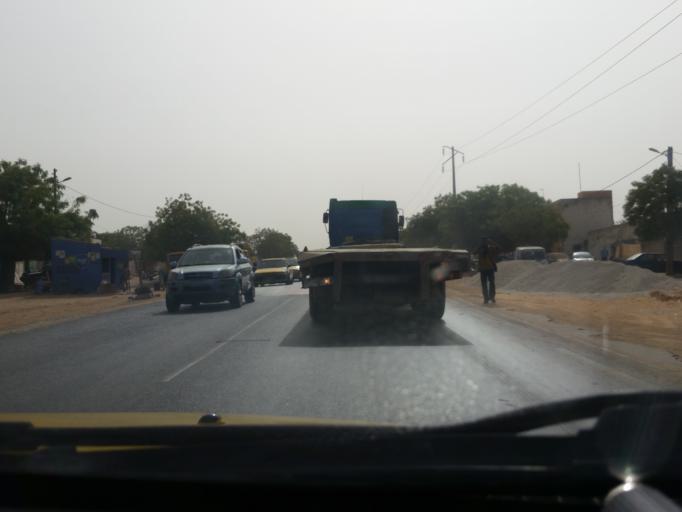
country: SN
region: Thies
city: Pout
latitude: 14.7367
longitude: -17.1470
